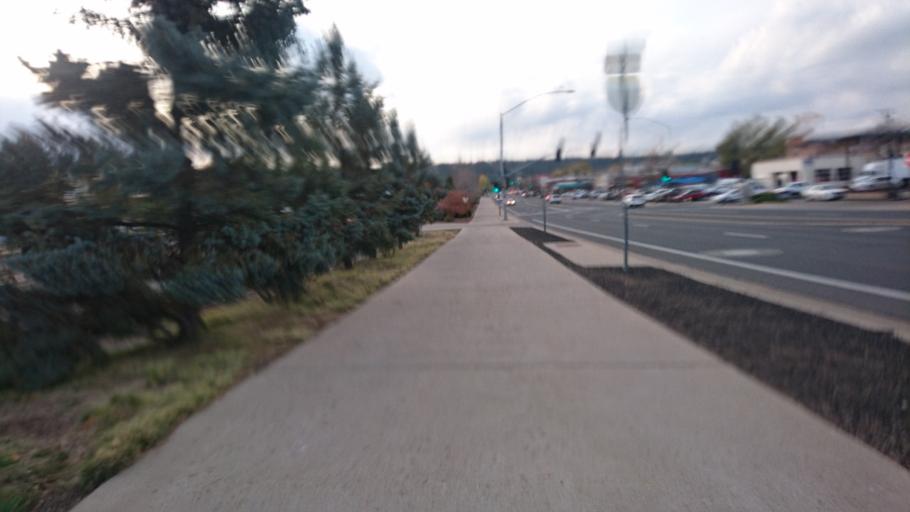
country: US
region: Arizona
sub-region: Coconino County
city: Flagstaff
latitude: 35.1962
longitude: -111.6452
